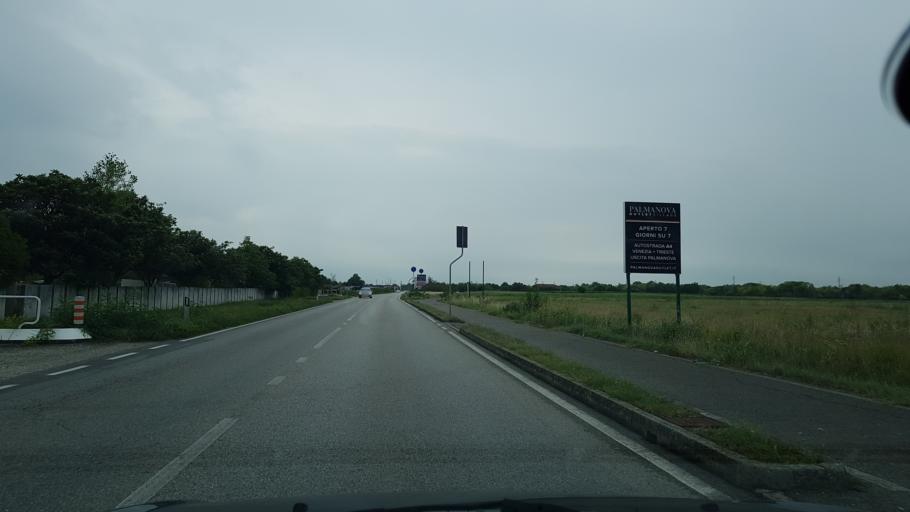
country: IT
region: Friuli Venezia Giulia
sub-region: Provincia di Udine
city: San Giovanni al Natisone
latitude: 45.9606
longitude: 13.3967
